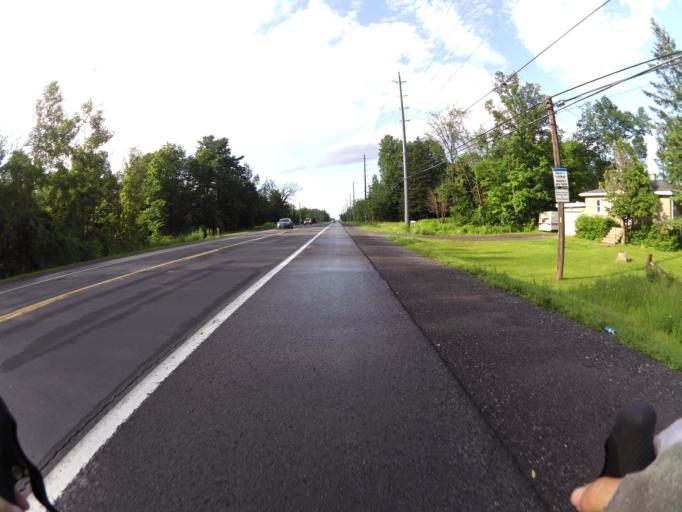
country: CA
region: Ontario
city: Bells Corners
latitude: 45.2865
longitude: -75.8373
